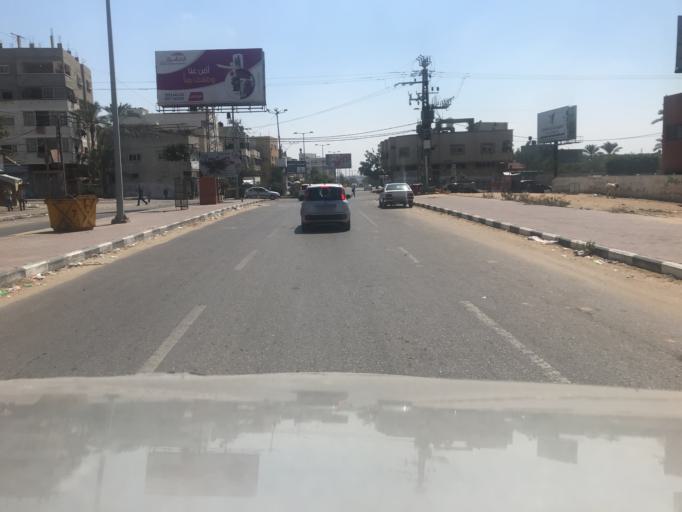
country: PS
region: Gaza Strip
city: Bayt Lahya
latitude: 31.5480
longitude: 34.4746
